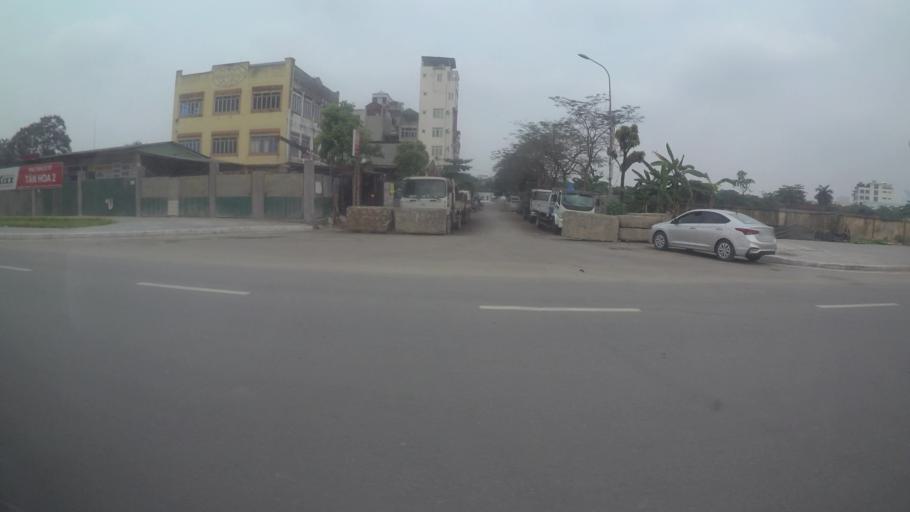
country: VN
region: Ha Noi
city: Cau Dien
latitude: 21.0475
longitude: 105.7359
